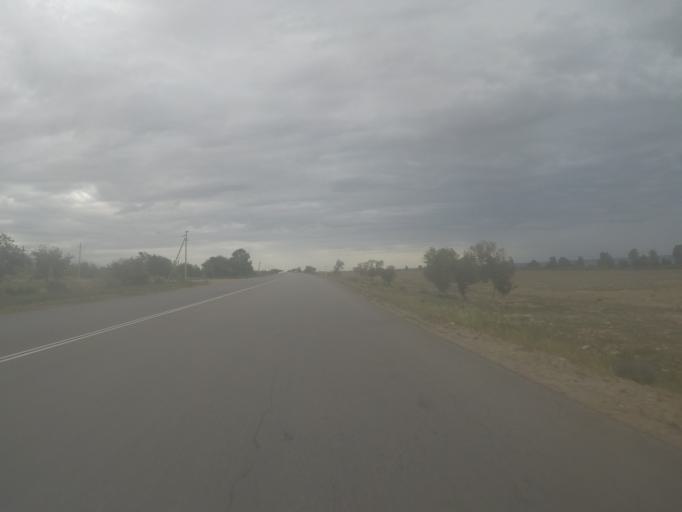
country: KG
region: Ysyk-Koel
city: Cholpon-Ata
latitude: 42.5975
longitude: 76.8102
